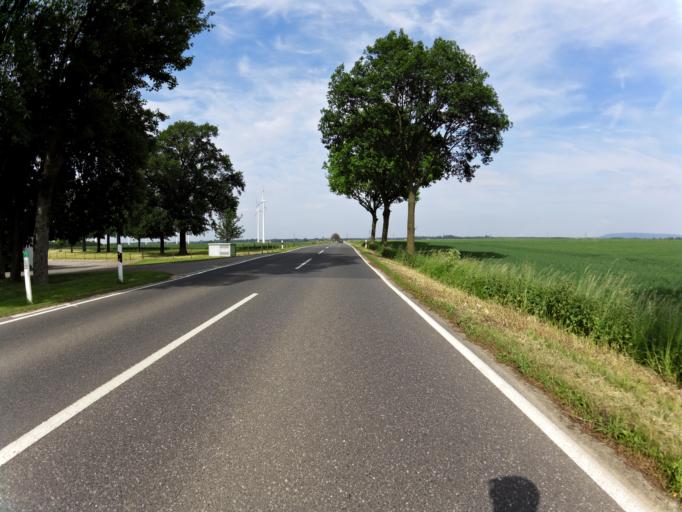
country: DE
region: North Rhine-Westphalia
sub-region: Regierungsbezirk Koln
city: Aldenhoven
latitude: 50.9175
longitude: 6.2773
